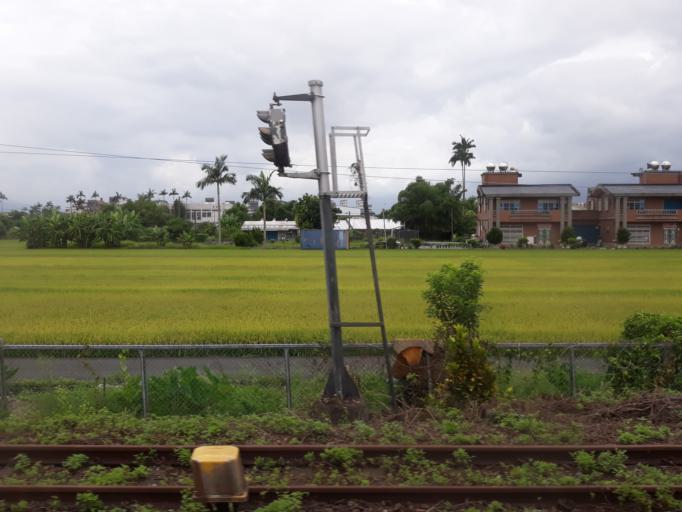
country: TW
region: Taiwan
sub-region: Yilan
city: Yilan
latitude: 24.7002
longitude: 121.7753
